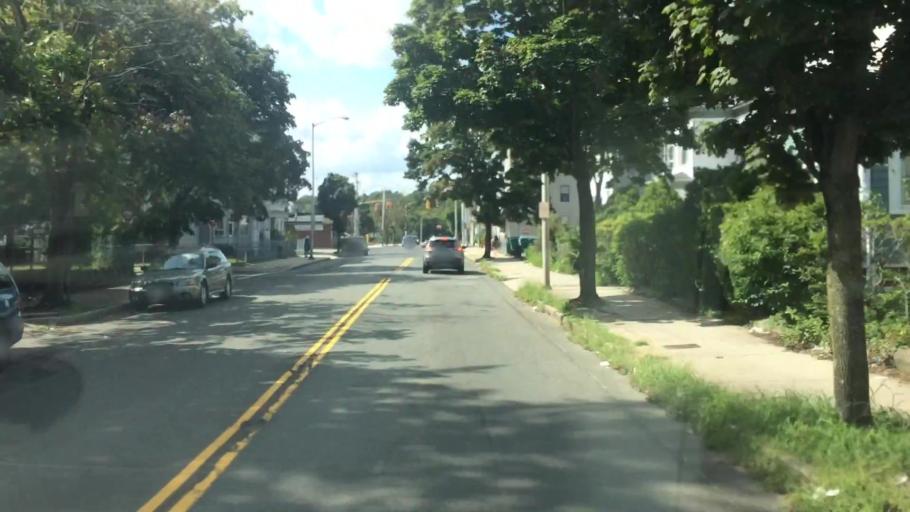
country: US
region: Massachusetts
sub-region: Essex County
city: Lynn
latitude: 42.4692
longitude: -70.9558
